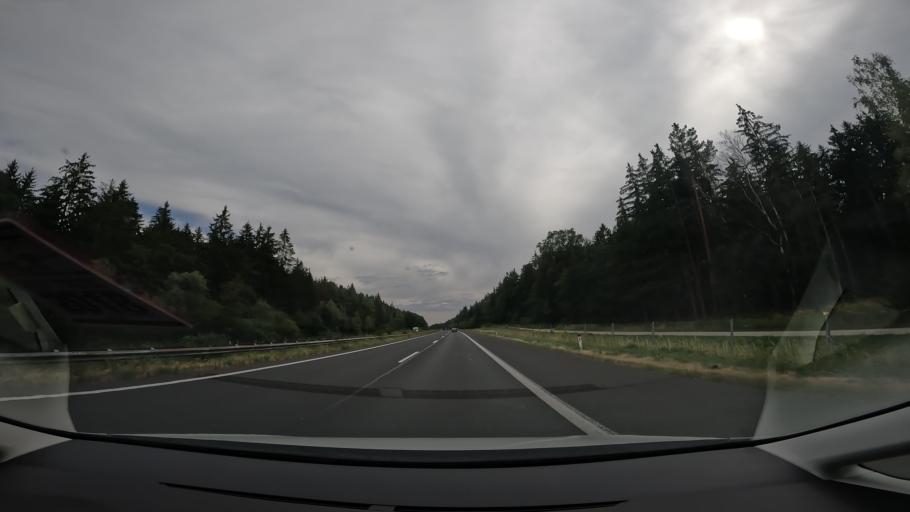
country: AT
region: Styria
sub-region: Politischer Bezirk Hartberg-Fuerstenfeld
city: Bad Waltersdorf
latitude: 47.1308
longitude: 15.9815
